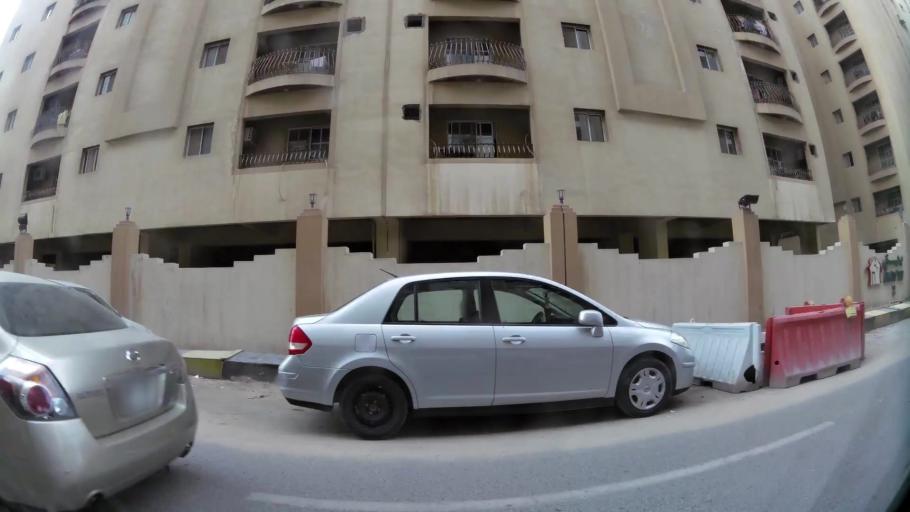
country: QA
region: Baladiyat ad Dawhah
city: Doha
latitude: 25.2816
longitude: 51.5195
